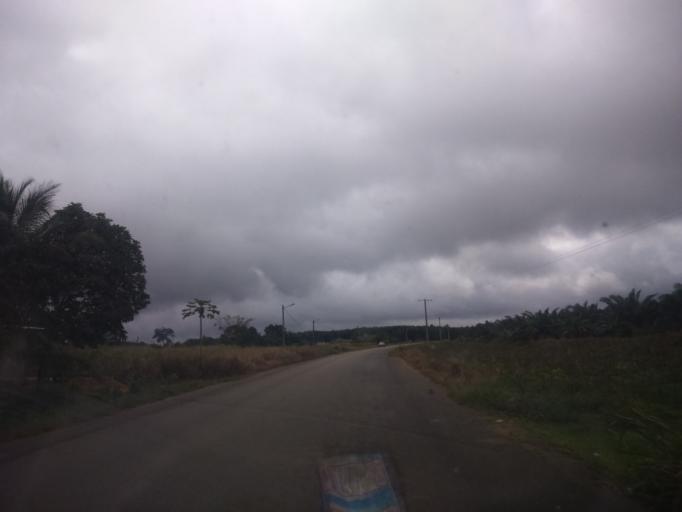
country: CI
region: Sud-Comoe
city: Adiake
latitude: 5.2968
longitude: -3.4375
